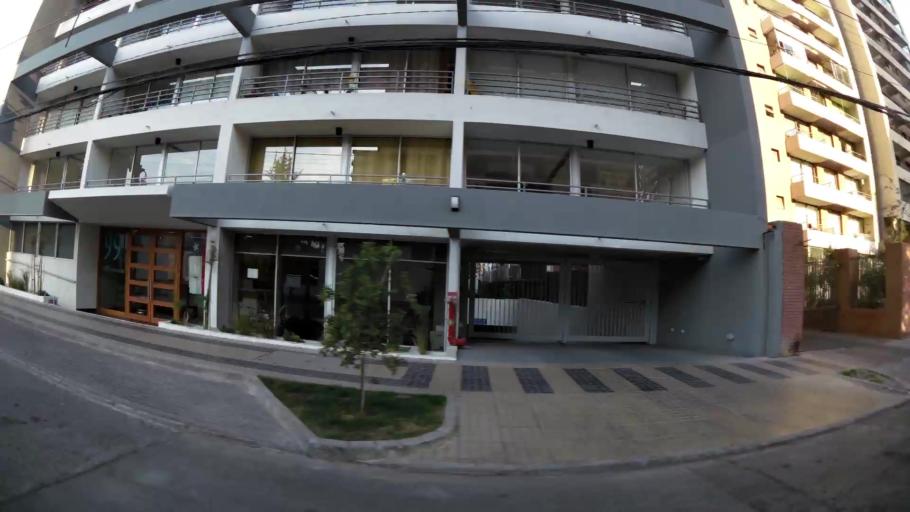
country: CL
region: Santiago Metropolitan
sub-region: Provincia de Santiago
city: Villa Presidente Frei, Nunoa, Santiago, Chile
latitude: -33.4548
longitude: -70.5765
